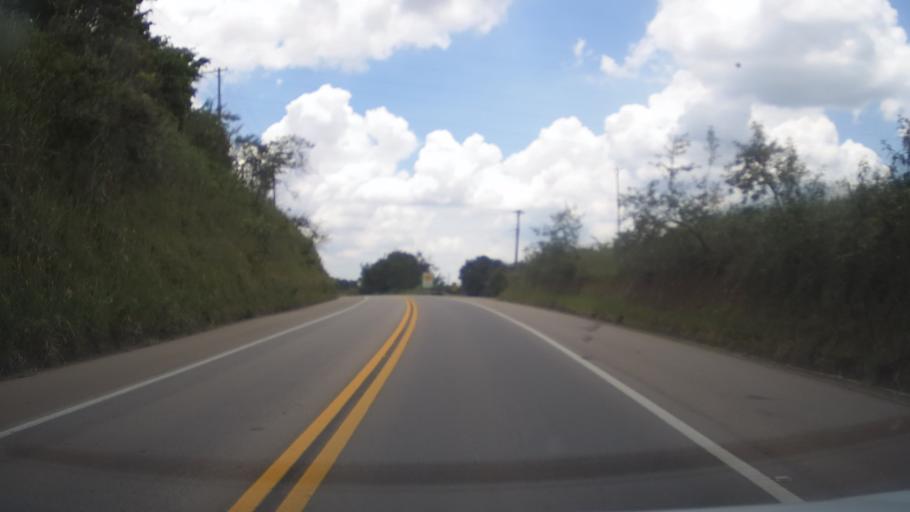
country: BR
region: Sao Paulo
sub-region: Vinhedo
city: Vinhedo
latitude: -23.0479
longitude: -46.9631
